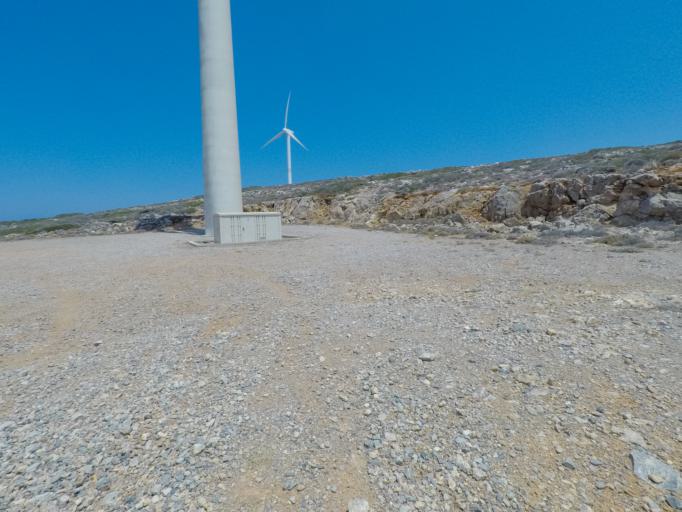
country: GR
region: Crete
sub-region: Nomos Lasithiou
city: Elounda
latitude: 35.3329
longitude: 25.7595
